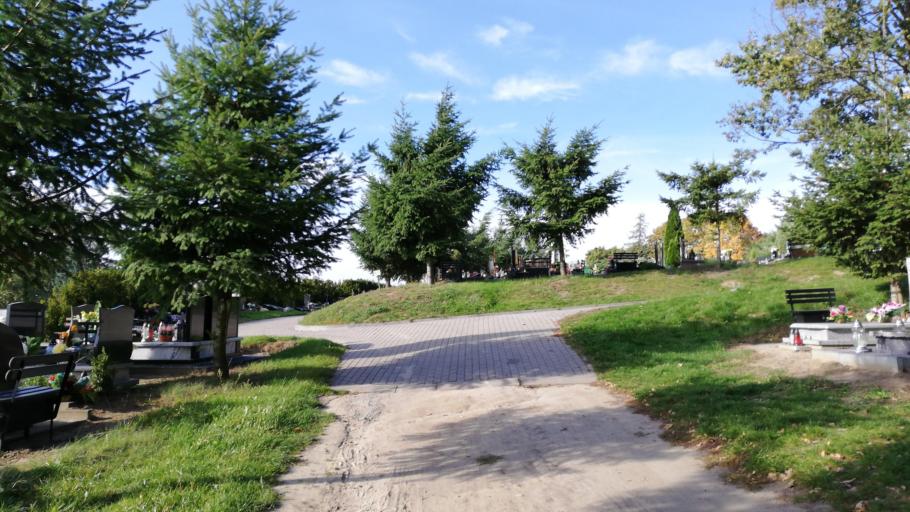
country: PL
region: West Pomeranian Voivodeship
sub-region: Powiat szczecinecki
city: Szczecinek
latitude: 53.7094
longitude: 16.7110
